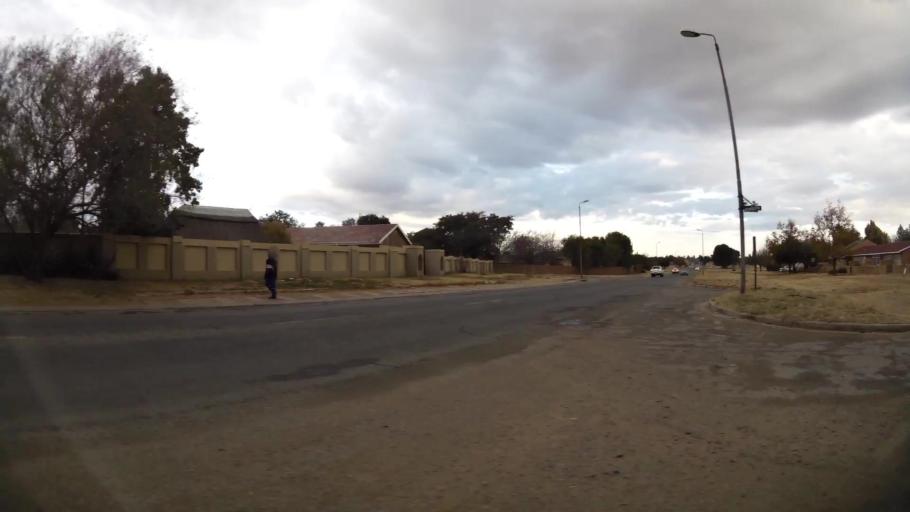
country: ZA
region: Orange Free State
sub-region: Lejweleputswa District Municipality
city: Welkom
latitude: -27.9638
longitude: 26.7258
